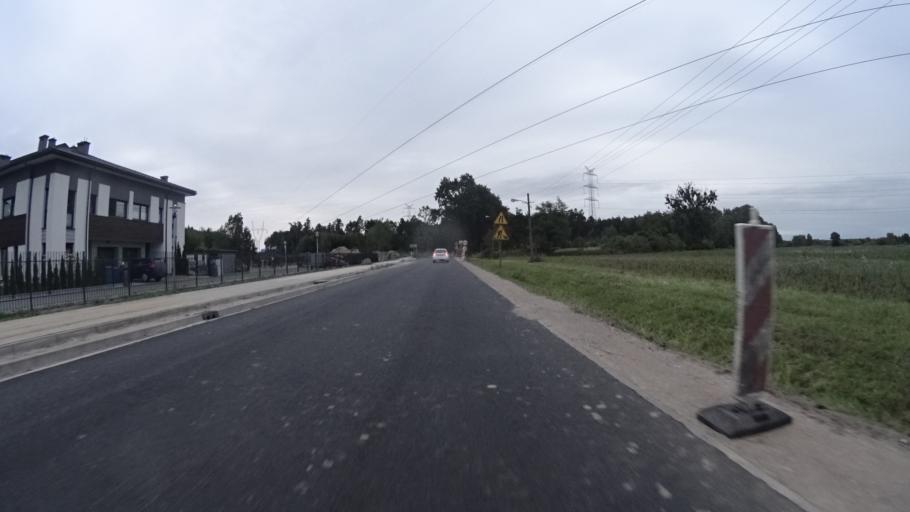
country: PL
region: Masovian Voivodeship
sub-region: Powiat warszawski zachodni
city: Stare Babice
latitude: 52.2697
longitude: 20.8317
